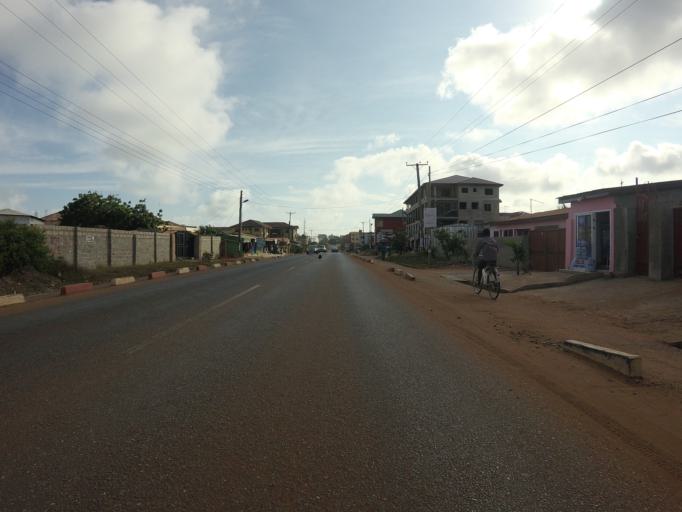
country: GH
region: Greater Accra
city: Teshi Old Town
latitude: 5.5746
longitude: -0.1397
